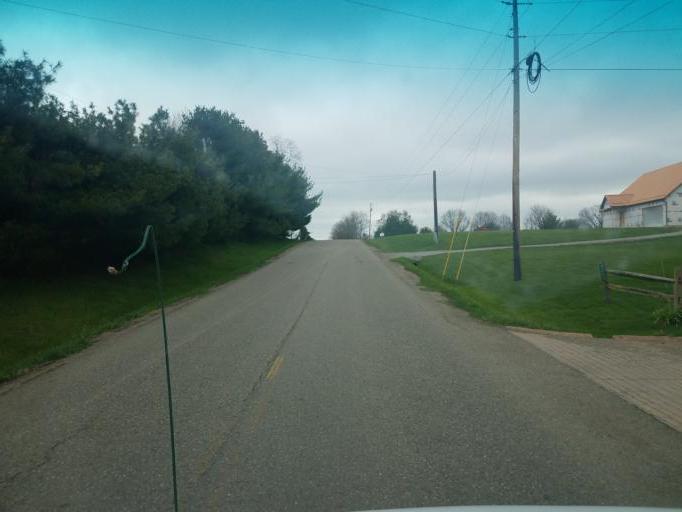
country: US
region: Ohio
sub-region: Stark County
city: Beach City
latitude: 40.6337
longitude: -81.6057
